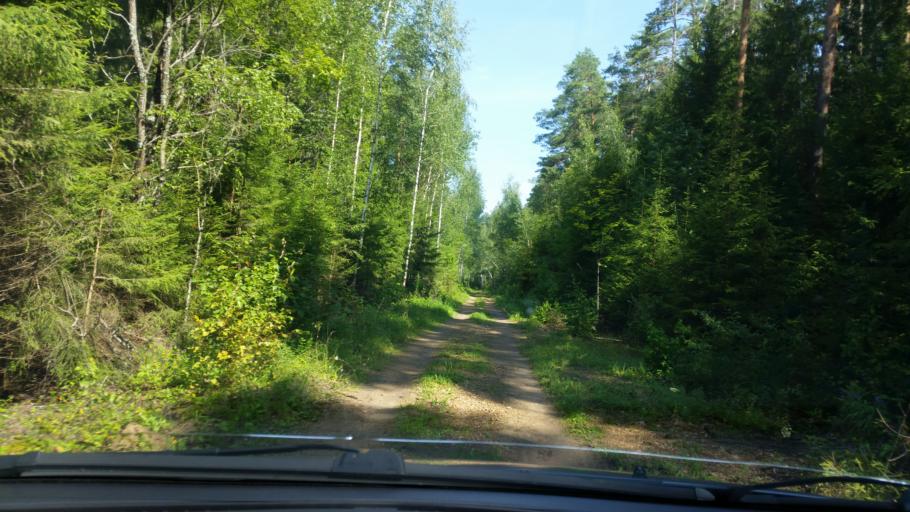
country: RU
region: Moskovskaya
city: Bol'shoye Gryzlovo
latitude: 54.9000
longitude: 37.7631
